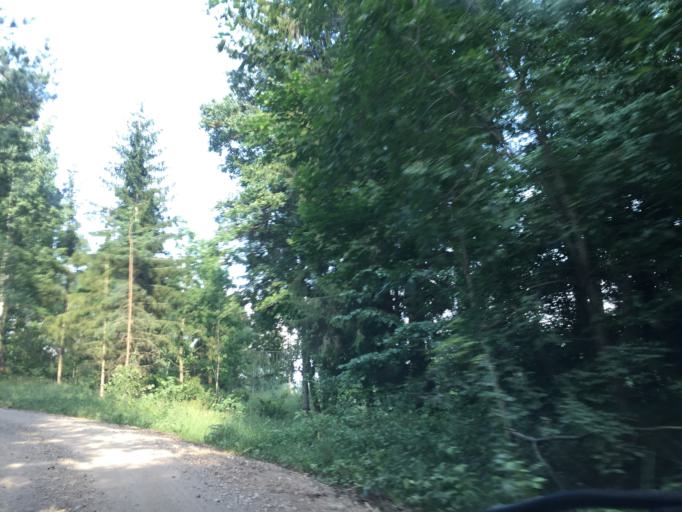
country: LT
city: Zagare
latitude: 56.4489
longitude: 23.1423
